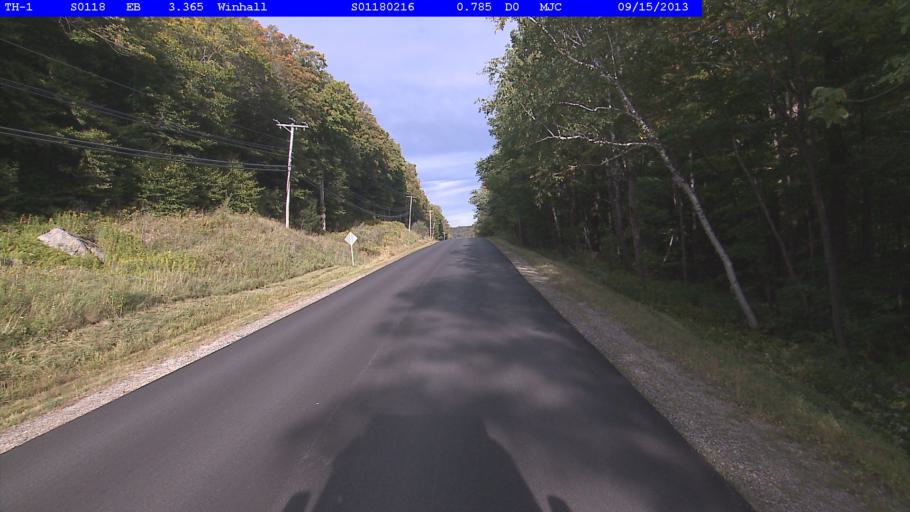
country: US
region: Vermont
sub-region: Bennington County
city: Manchester Center
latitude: 43.1253
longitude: -72.9106
